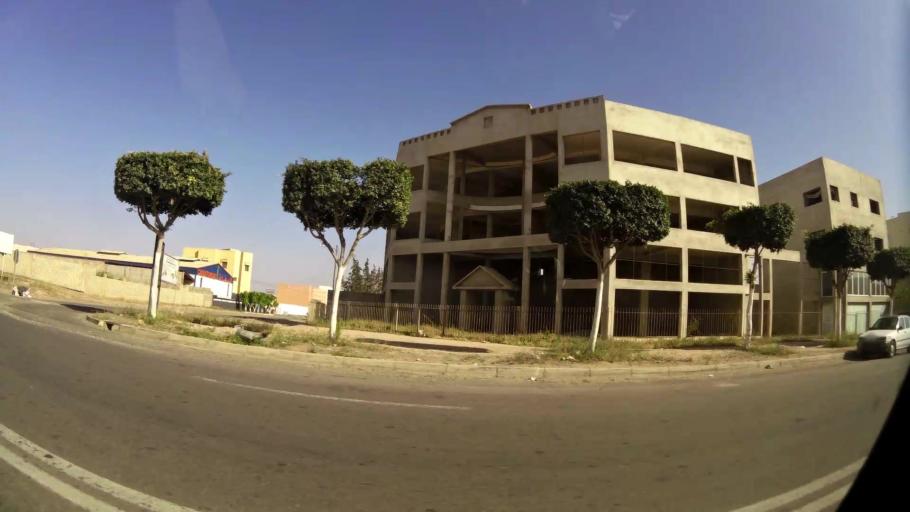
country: MA
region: Souss-Massa-Draa
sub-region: Inezgane-Ait Mellou
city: Inezgane
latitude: 30.3842
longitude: -9.5176
